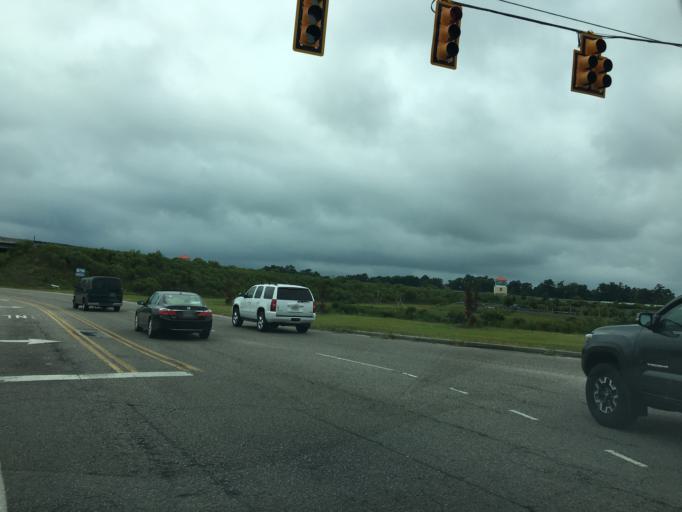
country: US
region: South Carolina
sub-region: Horry County
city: North Myrtle Beach
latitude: 33.7878
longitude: -78.7735
